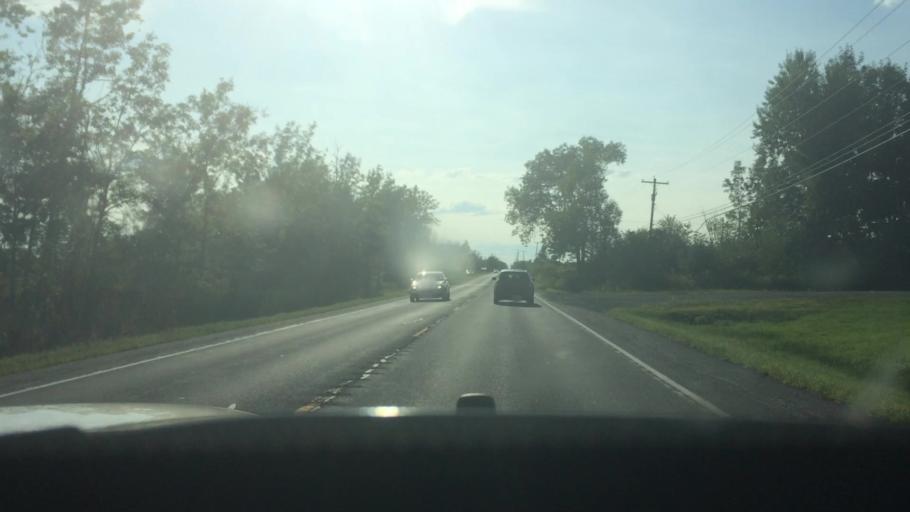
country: US
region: New York
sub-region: St. Lawrence County
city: Potsdam
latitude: 44.6700
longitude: -74.9459
